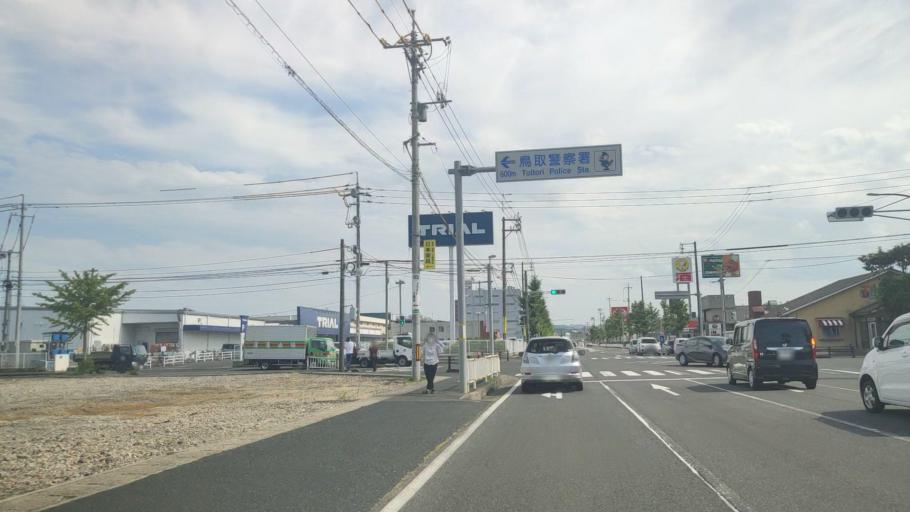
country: JP
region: Tottori
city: Tottori
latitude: 35.5175
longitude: 134.1922
